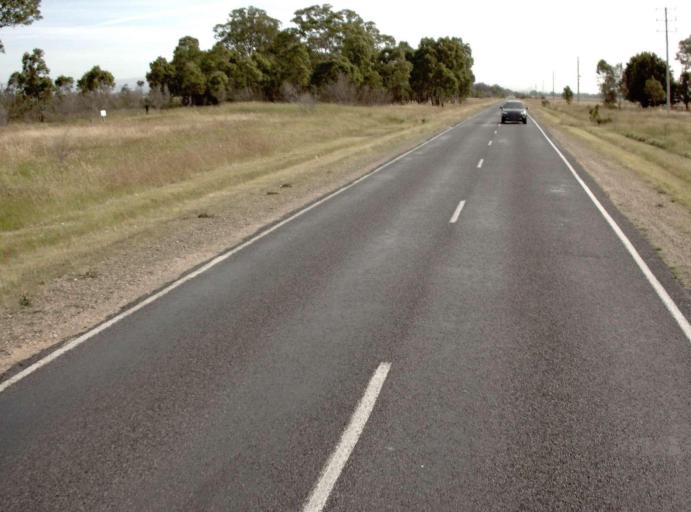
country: AU
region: Victoria
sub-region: Latrobe
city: Traralgon
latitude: -38.0763
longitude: 146.6110
